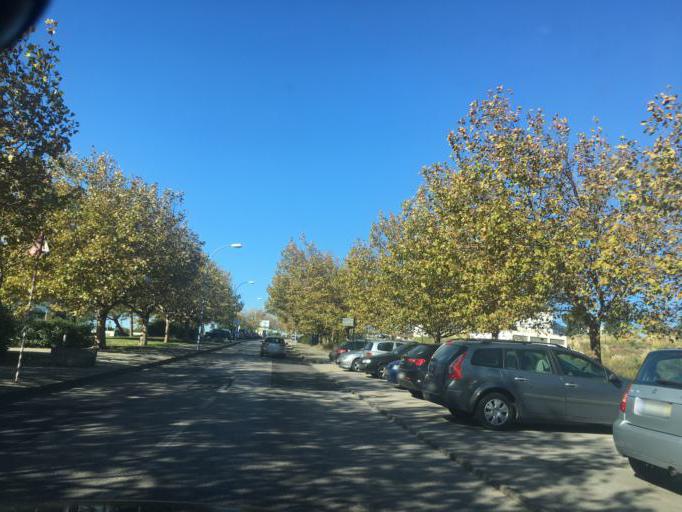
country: PT
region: Lisbon
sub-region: Oeiras
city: Porto Salvo
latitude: 38.7360
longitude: -9.2997
